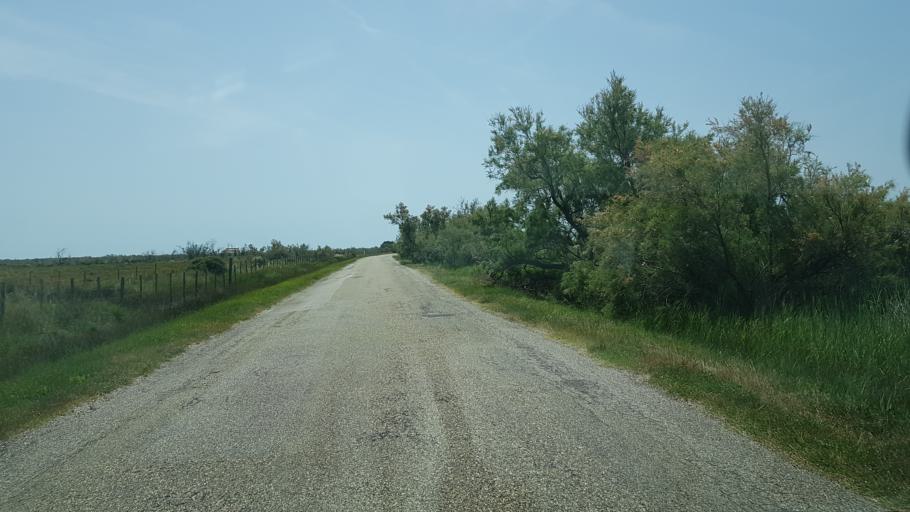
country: FR
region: Provence-Alpes-Cote d'Azur
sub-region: Departement des Bouches-du-Rhone
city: Arles
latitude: 43.4888
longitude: 4.6431
